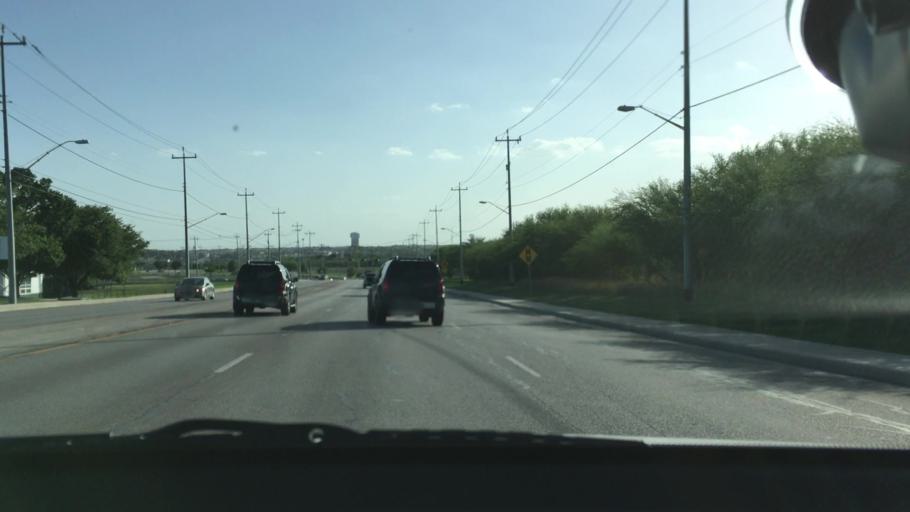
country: US
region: Texas
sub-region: Bexar County
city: Live Oak
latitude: 29.5452
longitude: -98.3183
